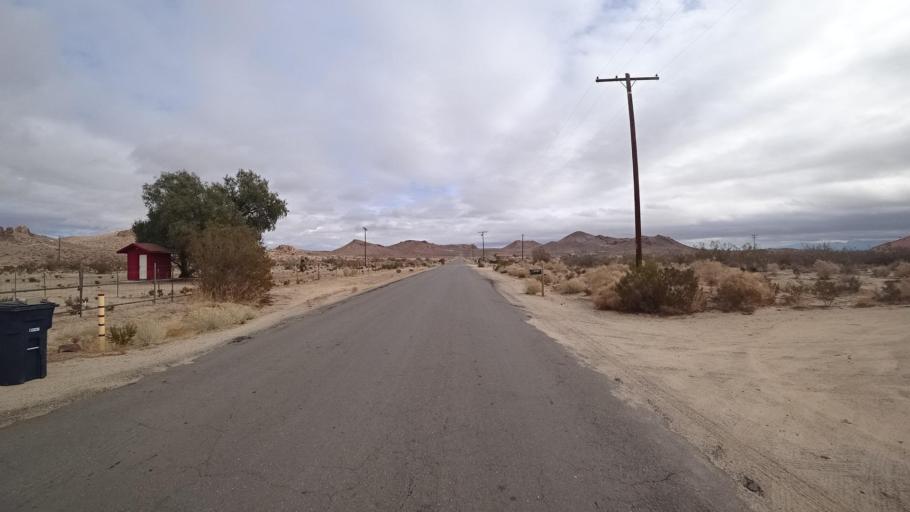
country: US
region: California
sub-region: Kern County
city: Rosamond
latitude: 34.8929
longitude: -118.2121
